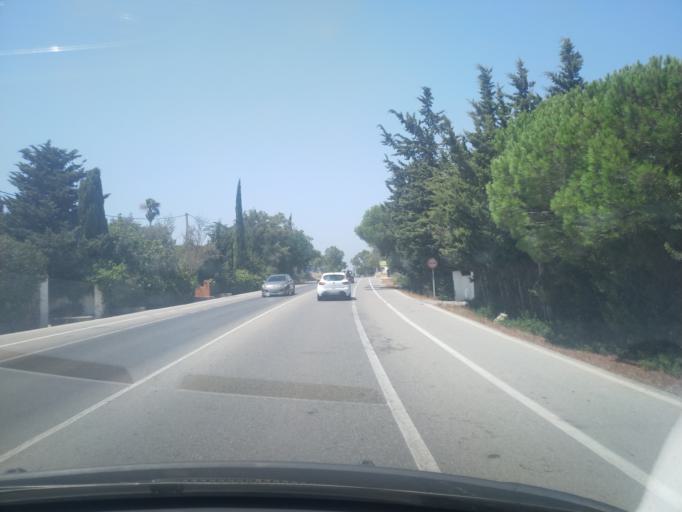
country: ES
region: Andalusia
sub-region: Provincia de Cadiz
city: Chiclana de la Frontera
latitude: 36.3914
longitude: -6.1430
